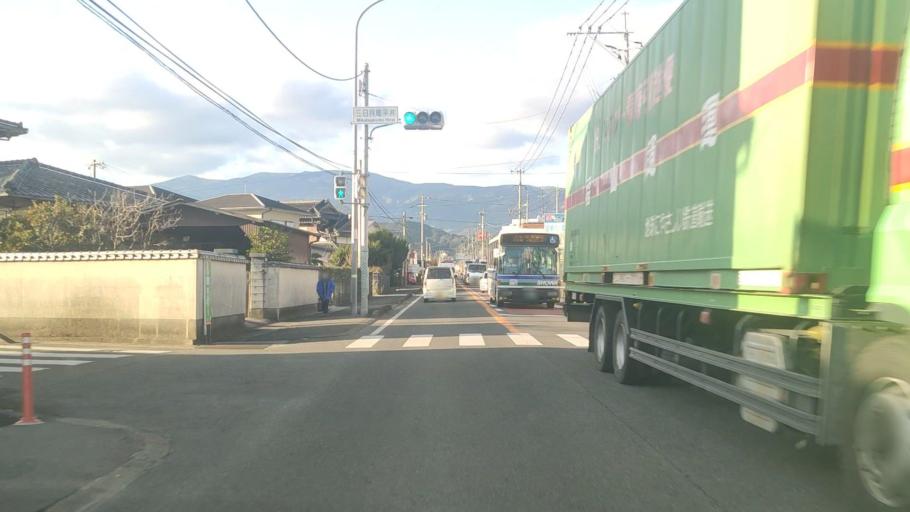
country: JP
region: Saga Prefecture
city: Saga-shi
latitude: 33.2877
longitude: 130.2067
